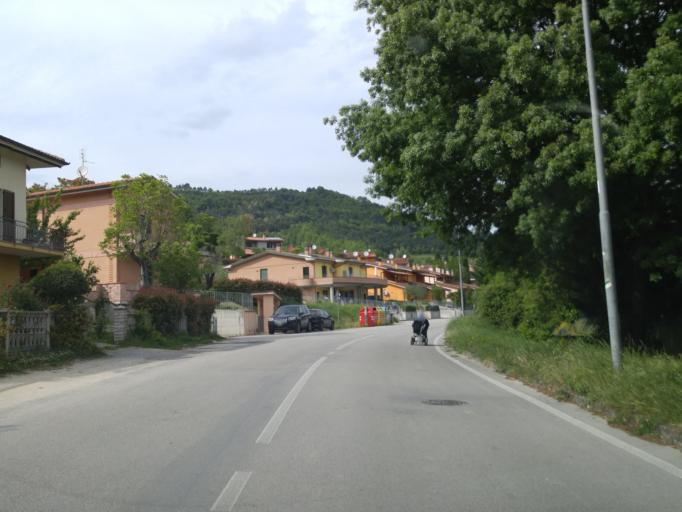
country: IT
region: The Marches
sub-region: Provincia di Pesaro e Urbino
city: Acqualagna
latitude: 43.6249
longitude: 12.6729
